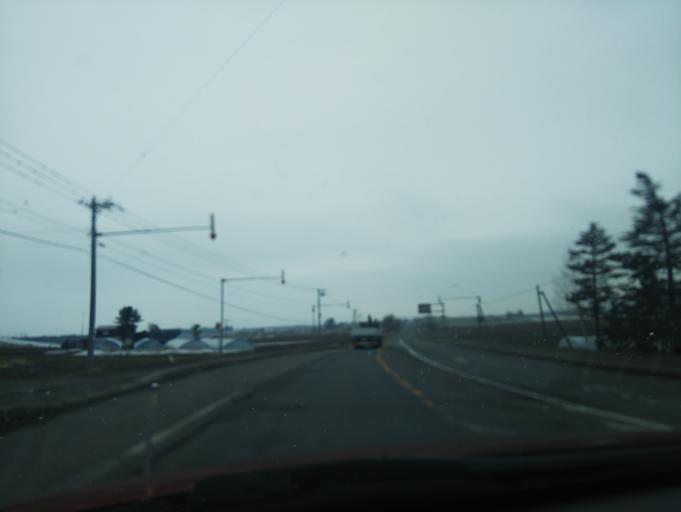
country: JP
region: Hokkaido
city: Nayoro
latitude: 44.0639
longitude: 142.3998
